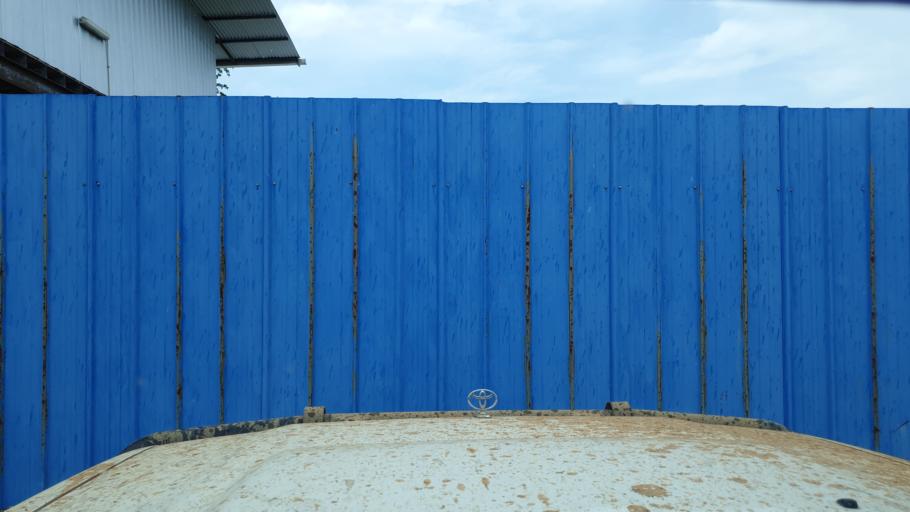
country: PG
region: Northern Province
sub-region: Sohe
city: Kokoda
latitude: -8.9420
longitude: 147.8678
